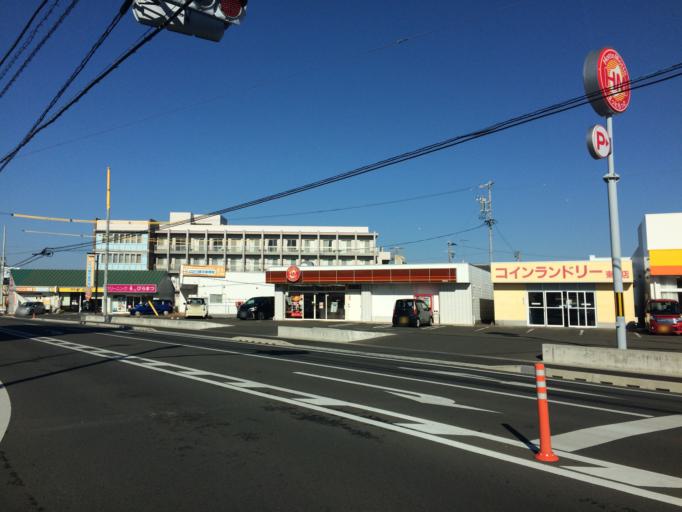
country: JP
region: Shizuoka
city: Shimada
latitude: 34.8328
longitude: 138.2213
